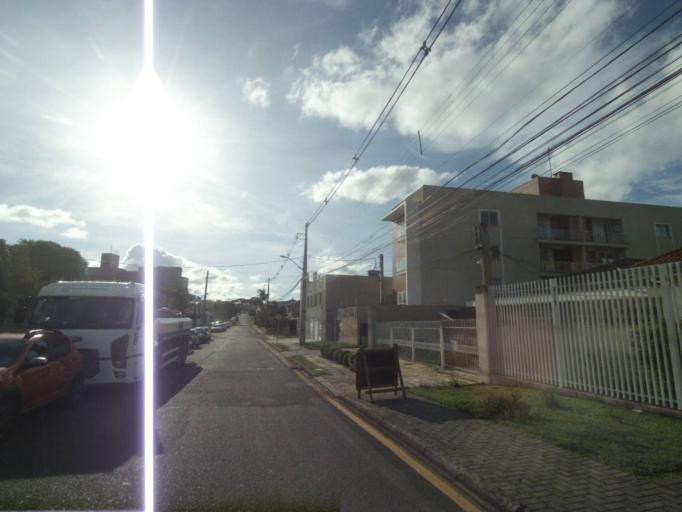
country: BR
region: Parana
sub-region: Curitiba
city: Curitiba
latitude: -25.4468
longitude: -49.3057
